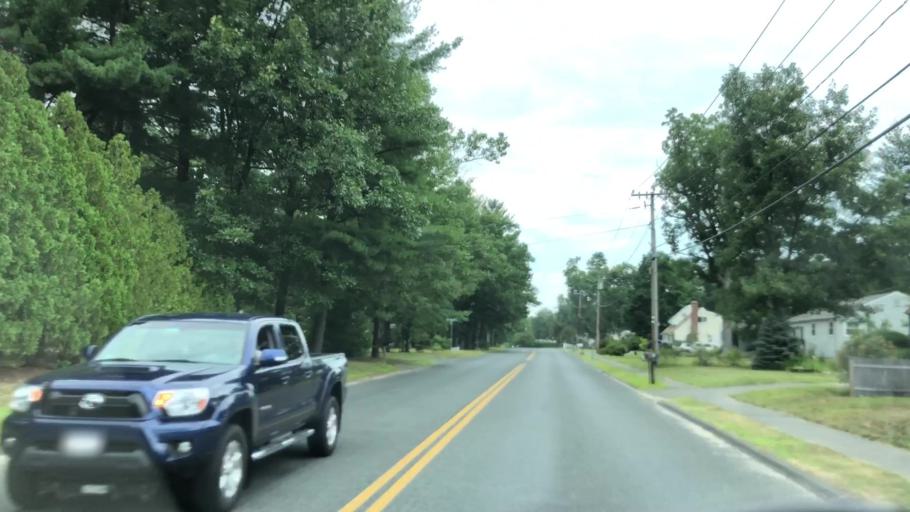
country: US
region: Massachusetts
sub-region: Hampshire County
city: Easthampton
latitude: 42.2298
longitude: -72.6860
